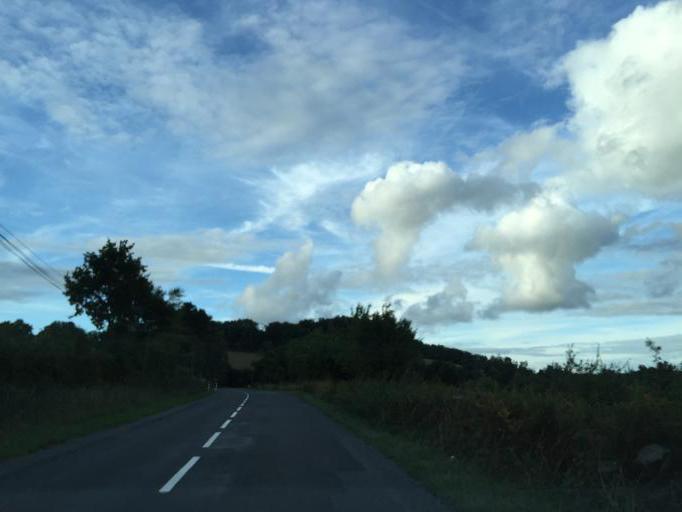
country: FR
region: Midi-Pyrenees
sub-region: Departement de l'Aveyron
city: Pont-de-Salars
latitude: 44.3006
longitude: 2.7317
